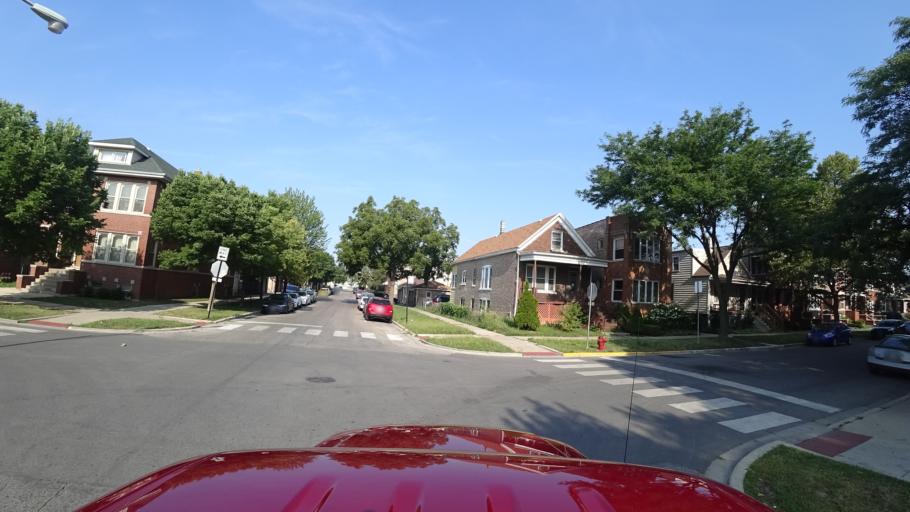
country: US
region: Illinois
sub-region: Cook County
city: Chicago
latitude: 41.8173
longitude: -87.6956
